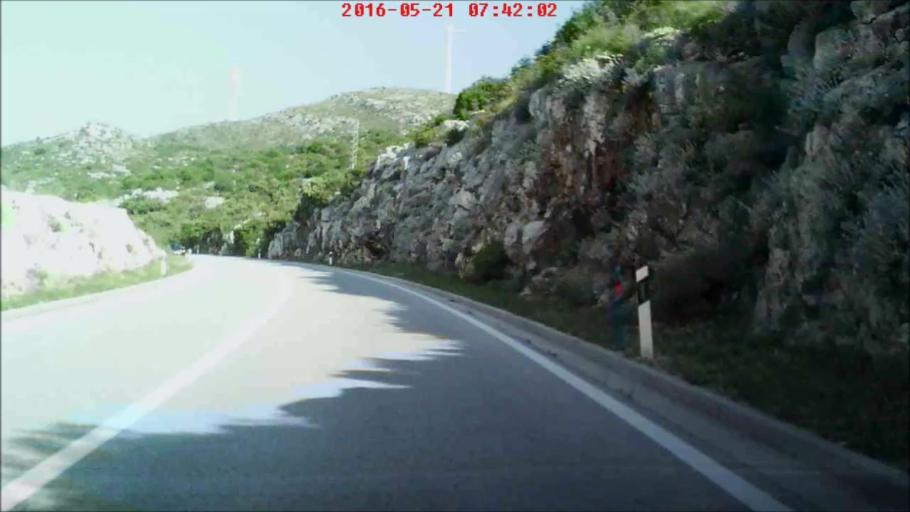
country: HR
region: Dubrovacko-Neretvanska
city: Podgora
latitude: 42.8084
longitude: 17.8091
